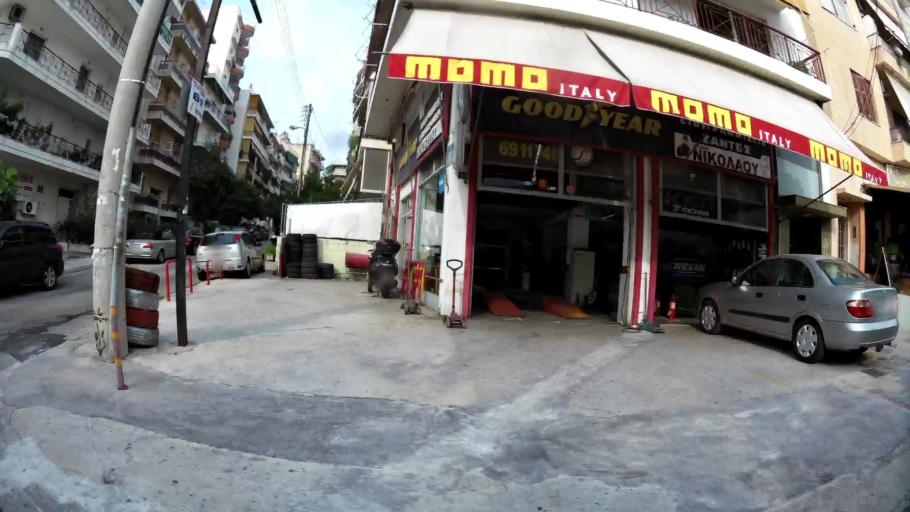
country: GR
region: Attica
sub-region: Nomarchia Athinas
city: Psychiko
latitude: 37.9966
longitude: 23.7629
